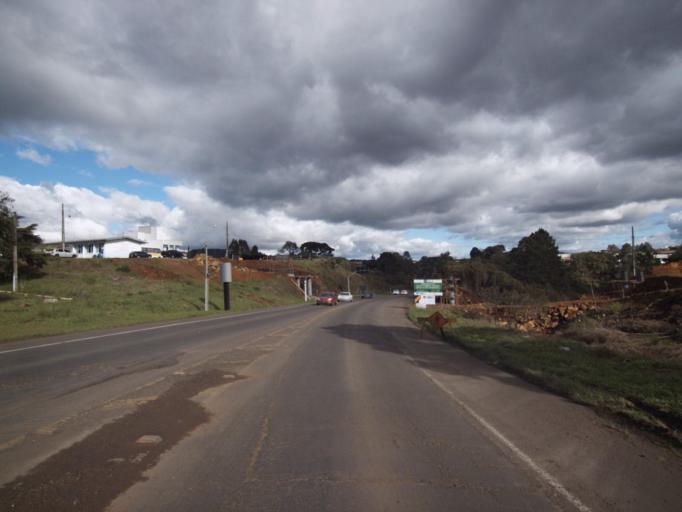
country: BR
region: Santa Catarina
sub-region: Joacaba
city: Joacaba
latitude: -27.0716
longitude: -51.6625
